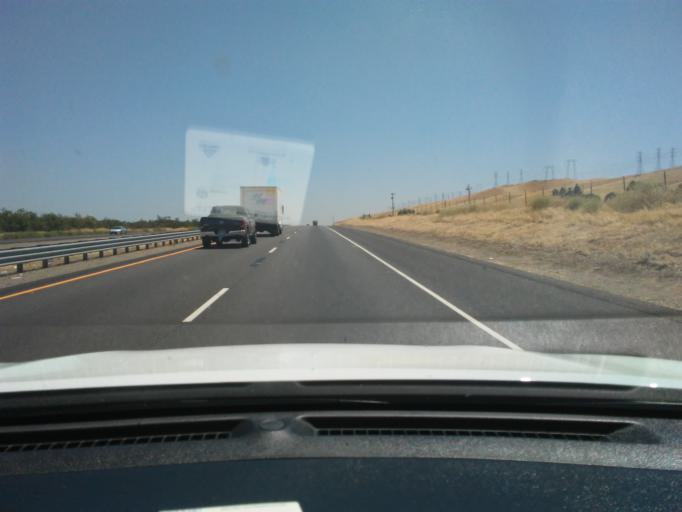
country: US
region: California
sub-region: Stanislaus County
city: Patterson
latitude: 37.5701
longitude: -121.3068
